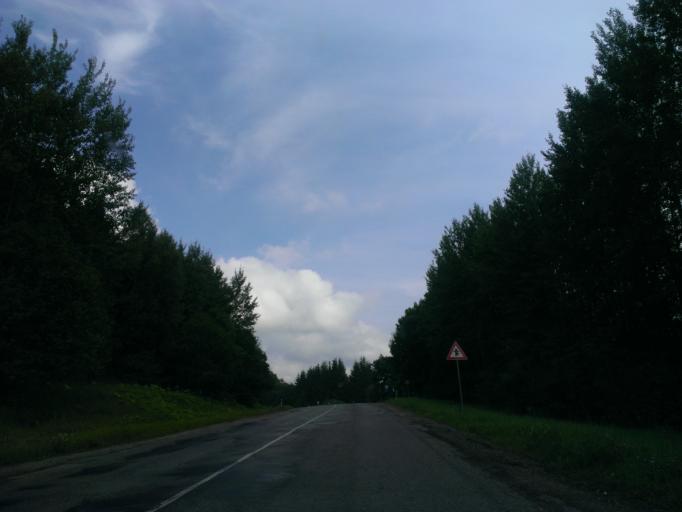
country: LV
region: Priekuli
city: Priekuli
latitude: 57.2687
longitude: 25.4623
